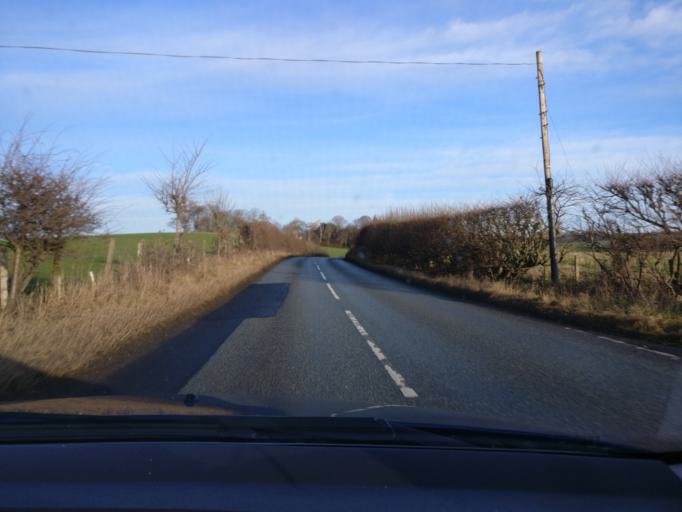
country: GB
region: Scotland
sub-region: The Scottish Borders
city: Kelso
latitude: 55.5310
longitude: -2.4690
